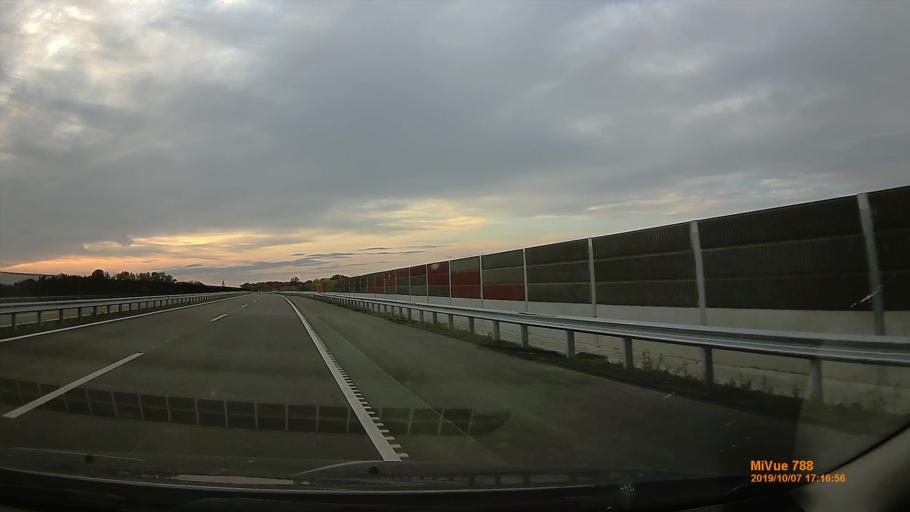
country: HU
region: Jasz-Nagykun-Szolnok
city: Kunszentmarton
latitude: 46.8616
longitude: 20.2994
